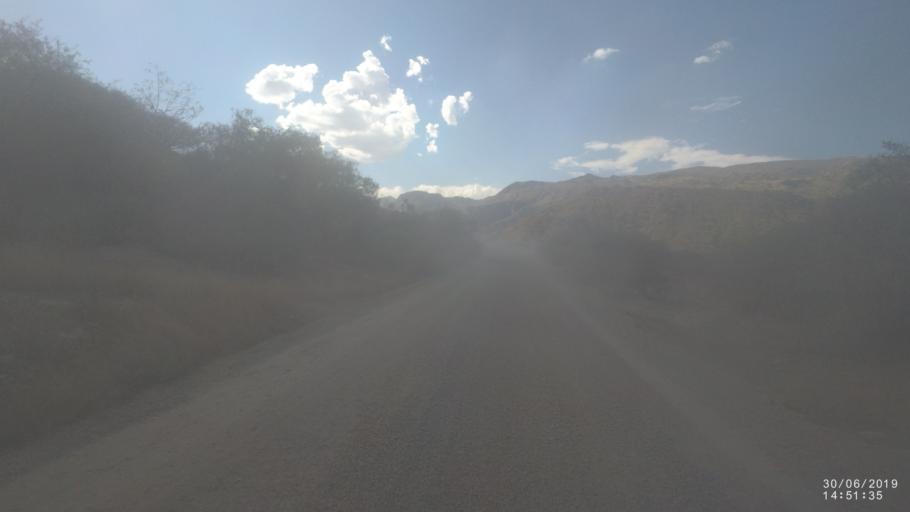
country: BO
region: Cochabamba
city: Irpa Irpa
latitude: -17.7714
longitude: -66.3434
